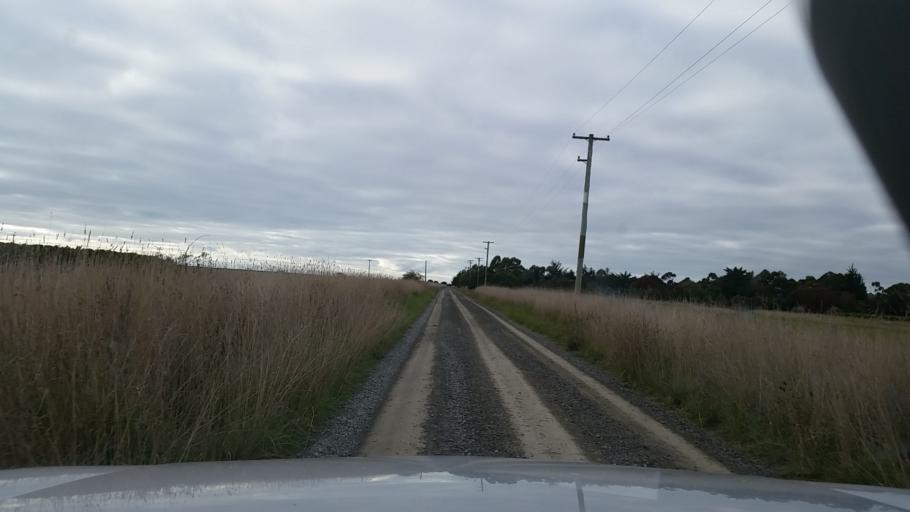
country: NZ
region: Marlborough
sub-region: Marlborough District
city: Blenheim
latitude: -41.5113
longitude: 174.0379
